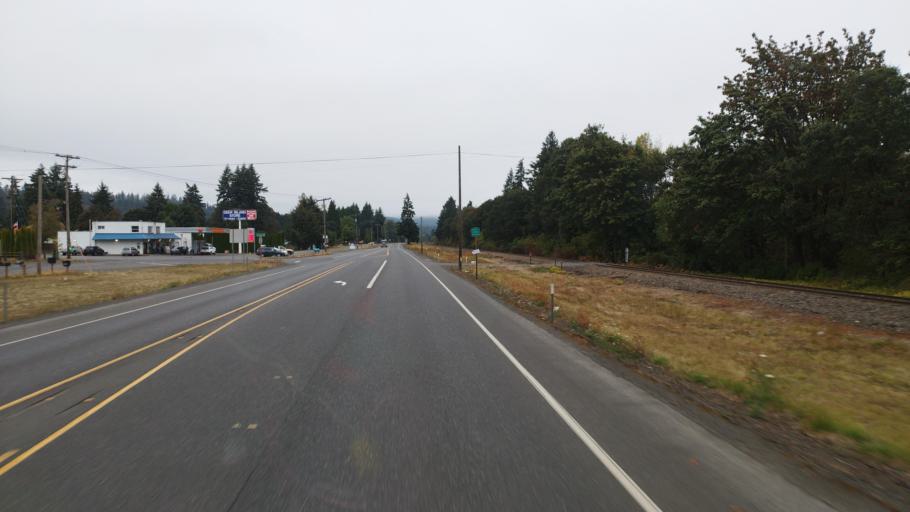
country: US
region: Oregon
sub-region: Columbia County
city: Columbia City
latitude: 45.9317
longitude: -122.8439
